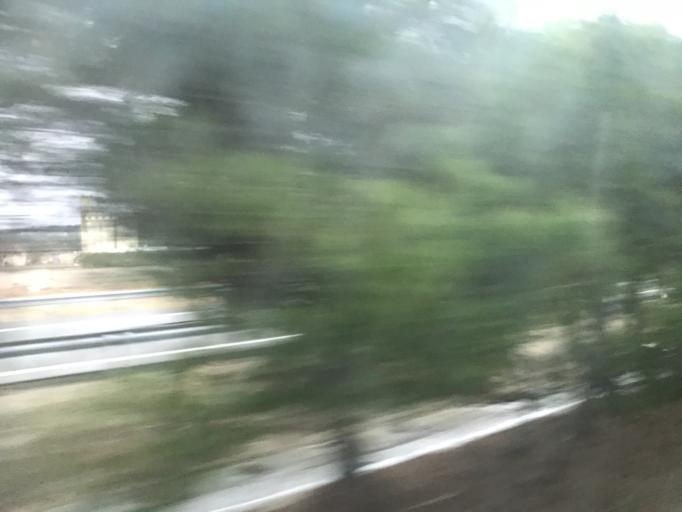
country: ES
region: Castille and Leon
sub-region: Provincia de Burgos
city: Villaquiran de los Infantes
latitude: 42.2174
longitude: -4.0058
